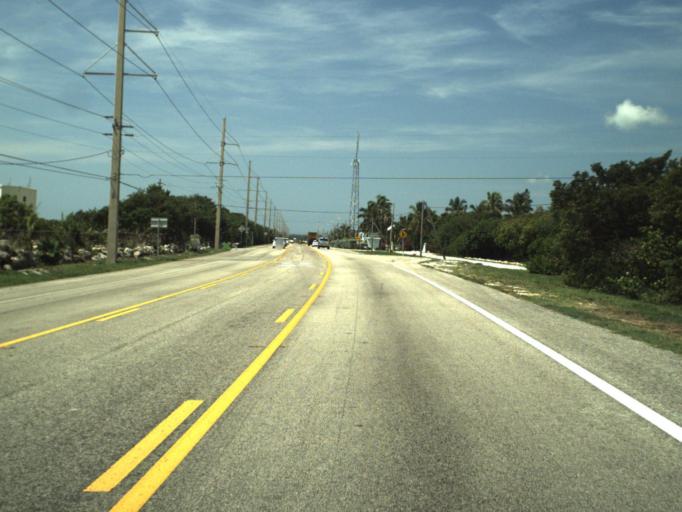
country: US
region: Florida
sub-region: Monroe County
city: Marathon
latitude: 24.7711
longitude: -80.9392
